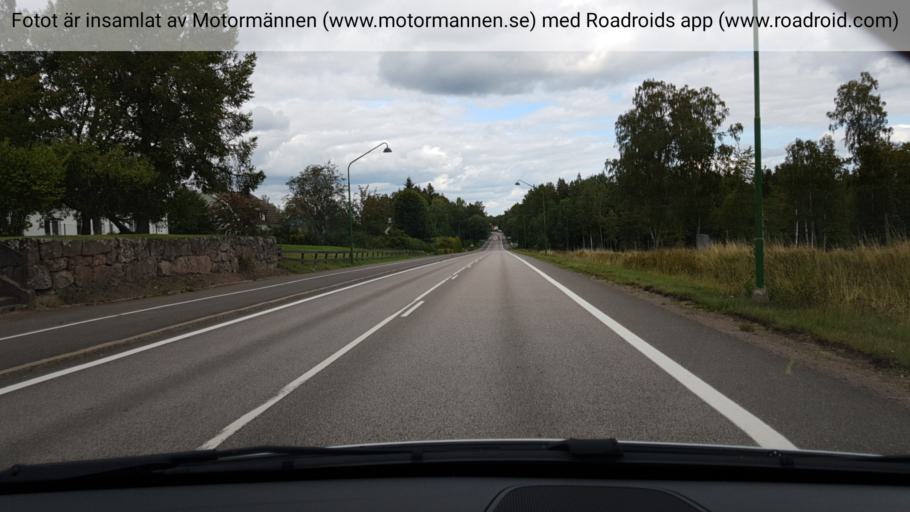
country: SE
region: Vaestra Goetaland
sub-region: Tidaholms Kommun
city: Tidaholm
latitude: 58.1661
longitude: 13.9411
